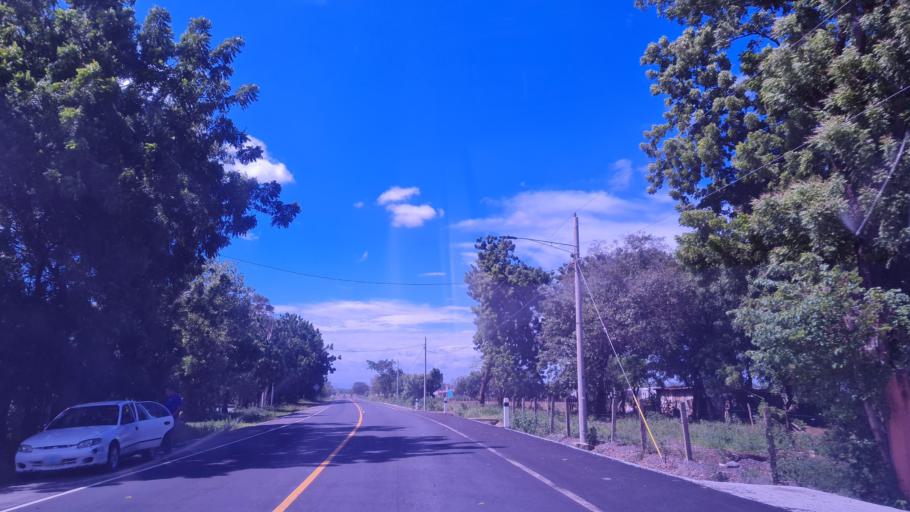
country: NI
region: Managua
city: Tipitapa
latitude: 12.1237
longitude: -86.1516
